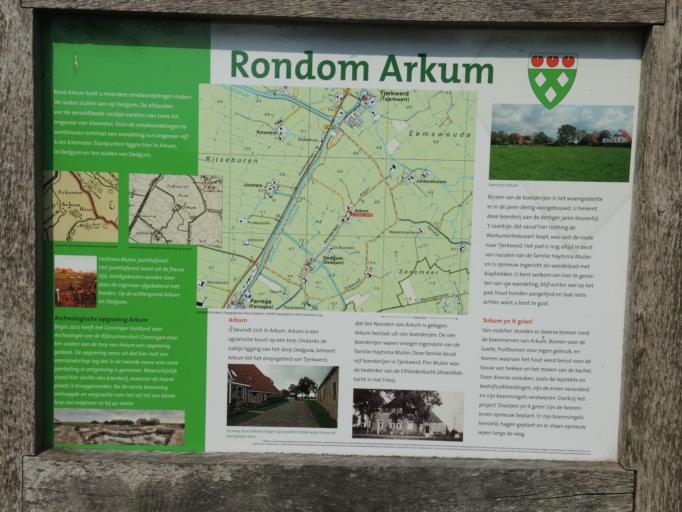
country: NL
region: Friesland
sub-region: Sudwest Fryslan
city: Bolsward
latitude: 53.0294
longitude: 5.4991
